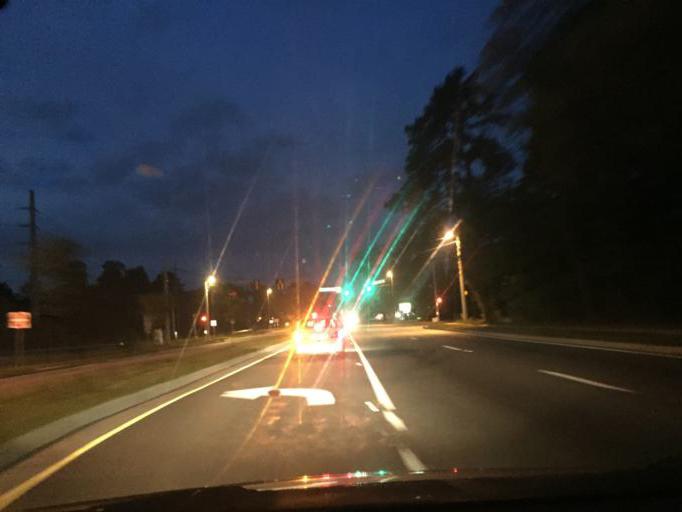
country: US
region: Georgia
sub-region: Chatham County
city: Montgomery
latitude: 31.9769
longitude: -81.1319
